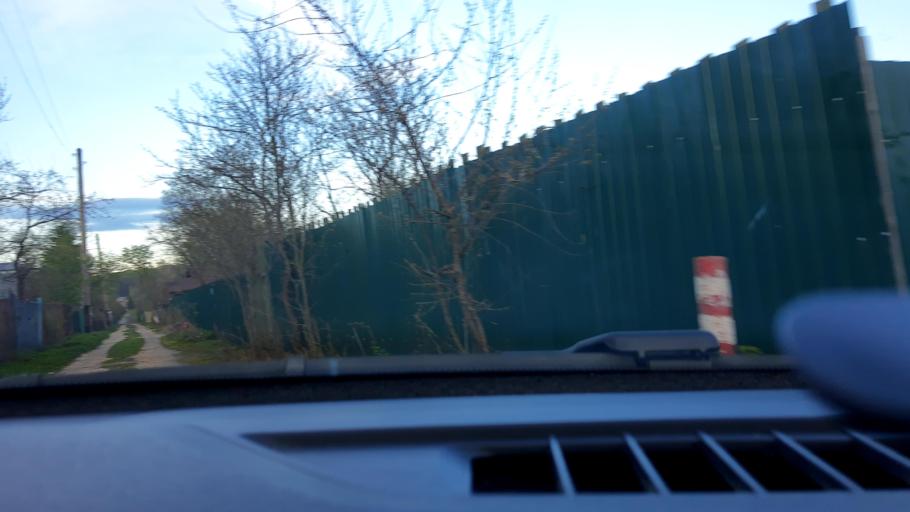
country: RU
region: Nizjnij Novgorod
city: Burevestnik
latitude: 56.1806
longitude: 43.7978
